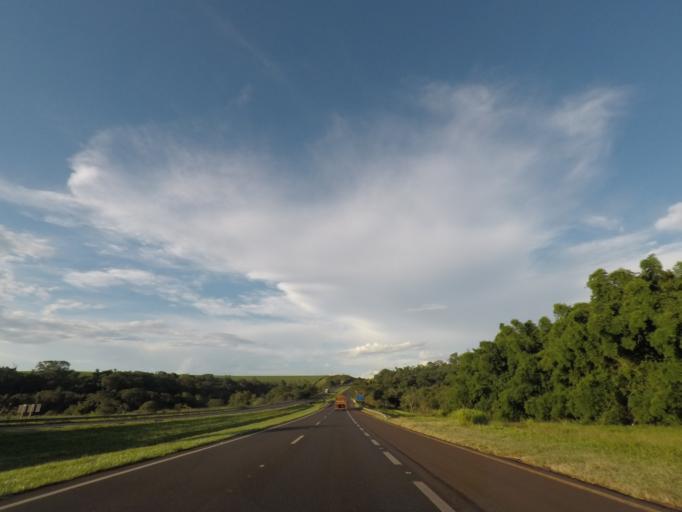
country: BR
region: Sao Paulo
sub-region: Ituverava
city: Ituverava
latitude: -20.2583
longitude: -47.7999
